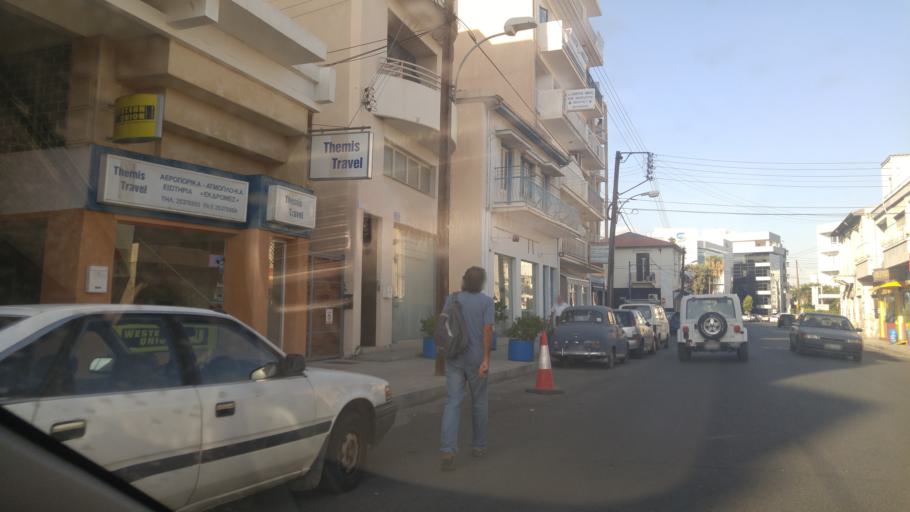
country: CY
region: Limassol
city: Limassol
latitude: 34.6816
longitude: 33.0457
